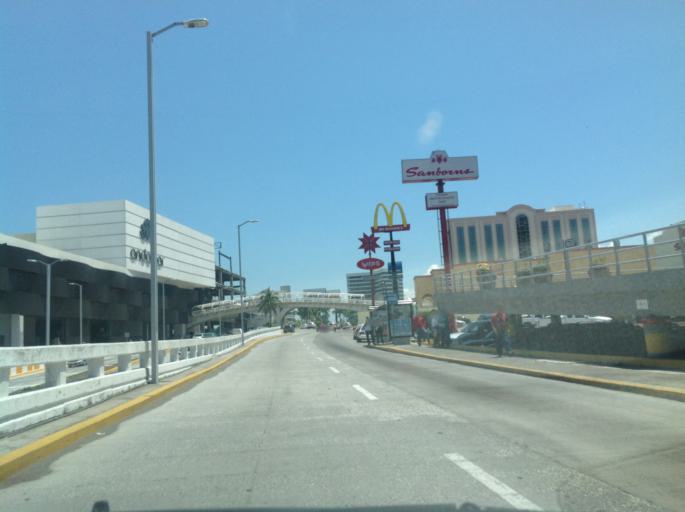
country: MX
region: Veracruz
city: Boca del Rio
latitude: 19.1405
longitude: -96.1039
